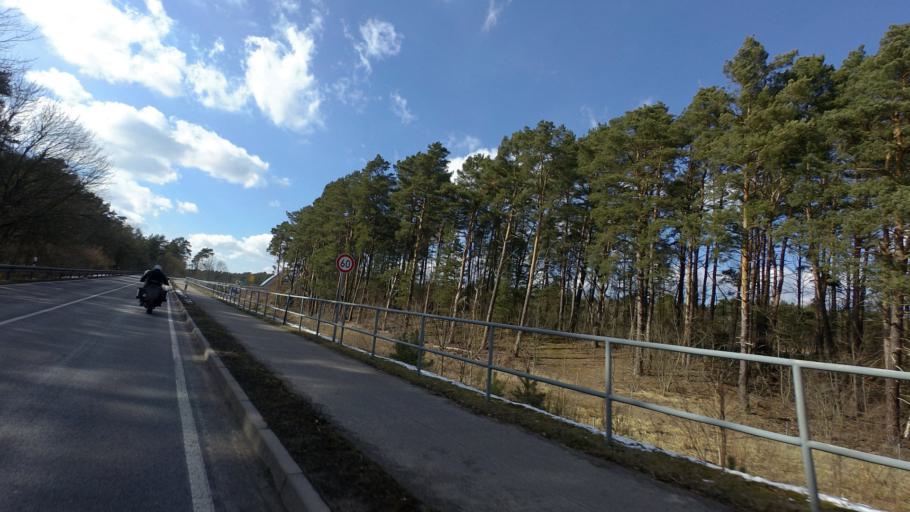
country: DE
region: Brandenburg
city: Marienwerder
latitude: 52.8542
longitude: 13.6545
